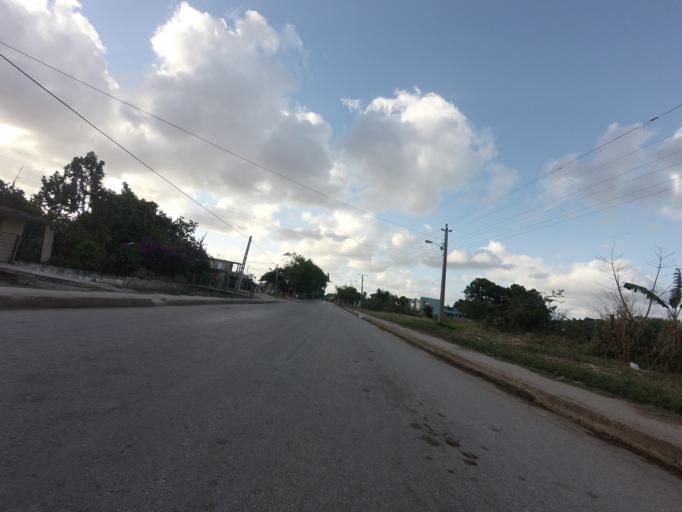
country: CU
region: Ciego de Avila
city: Ciego de Avila
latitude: 21.8291
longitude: -78.7521
